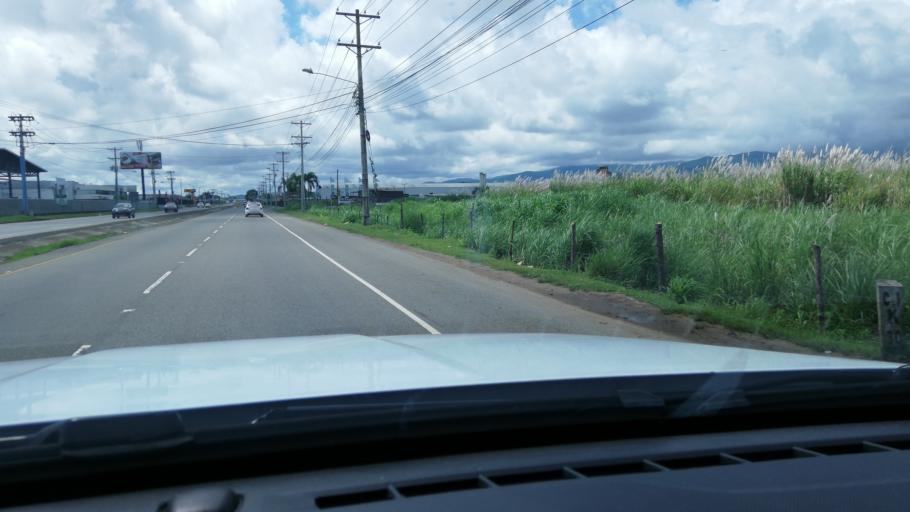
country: PA
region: Panama
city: Pacora
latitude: 9.0991
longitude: -79.3101
